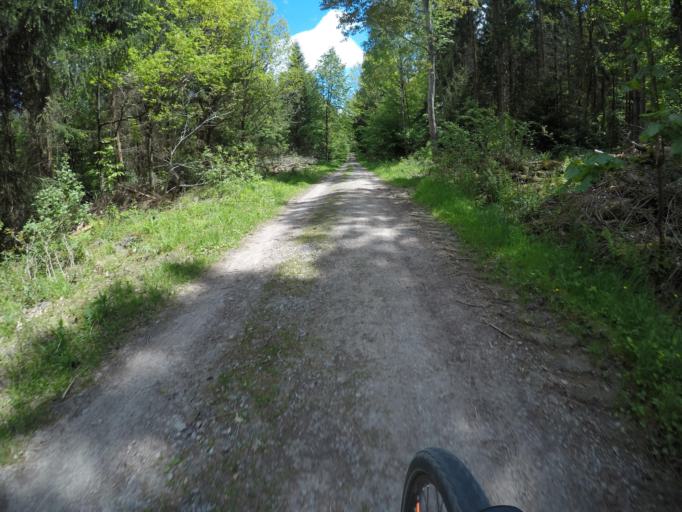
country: DE
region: Baden-Wuerttemberg
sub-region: Regierungsbezirk Stuttgart
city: Gerlingen
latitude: 48.7463
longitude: 9.0706
